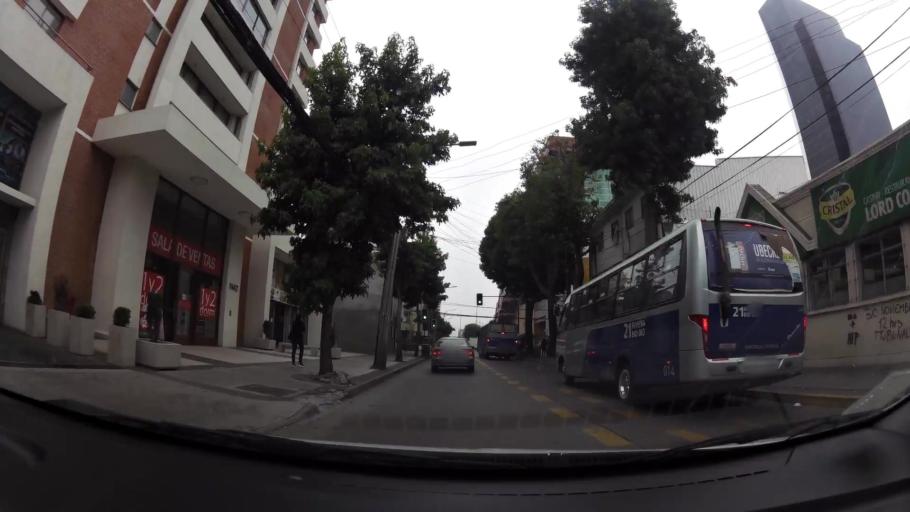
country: CL
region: Biobio
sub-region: Provincia de Concepcion
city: Concepcion
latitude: -36.8250
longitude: -73.0437
